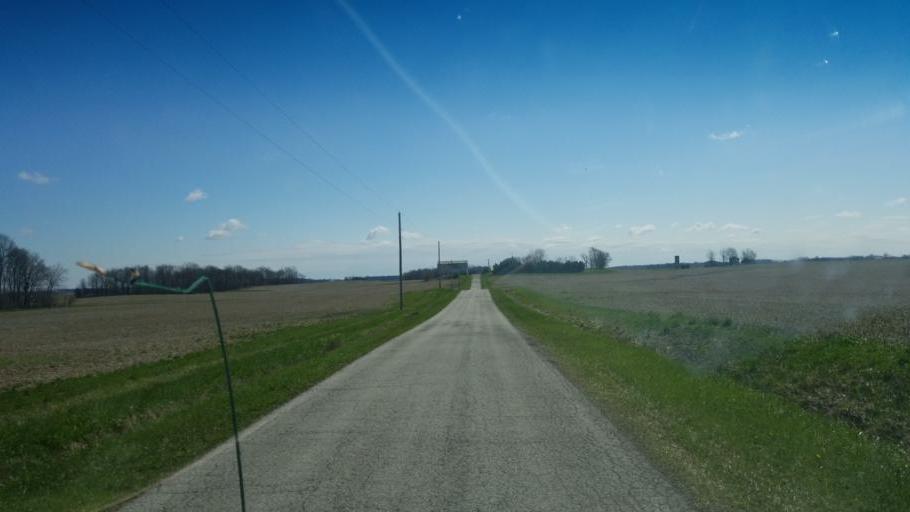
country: US
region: Ohio
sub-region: Crawford County
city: Bucyrus
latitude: 40.8668
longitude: -82.9278
